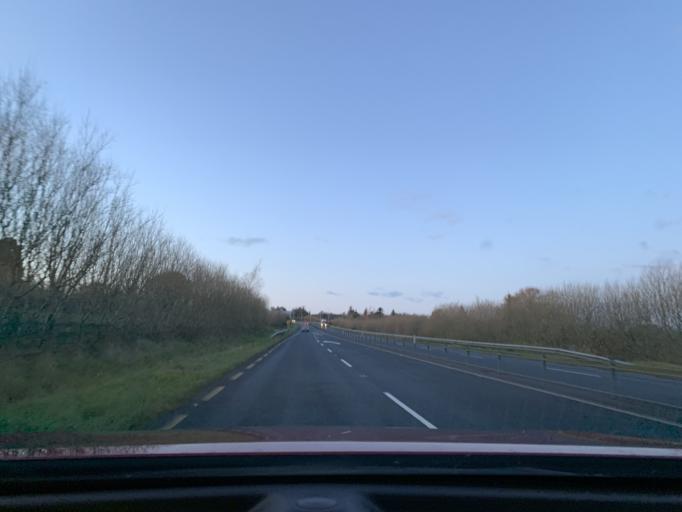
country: IE
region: Connaught
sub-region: County Leitrim
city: Carrick-on-Shannon
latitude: 53.8773
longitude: -7.9319
